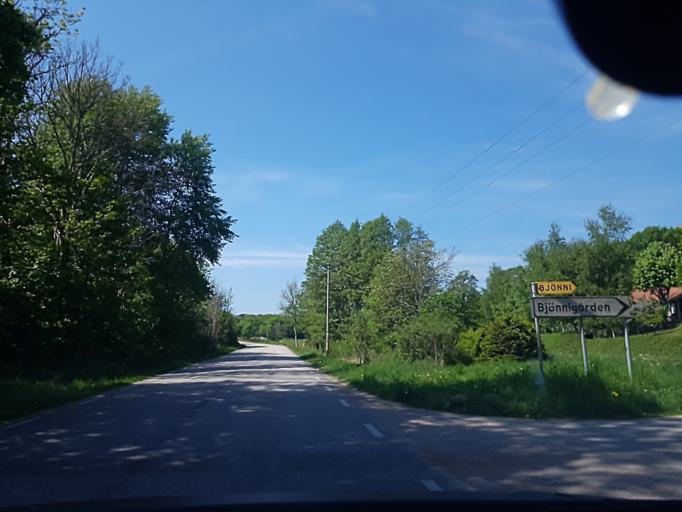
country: SE
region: Vaestra Goetaland
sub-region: Lysekils Kommun
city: Lysekil
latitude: 58.1631
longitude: 11.4509
